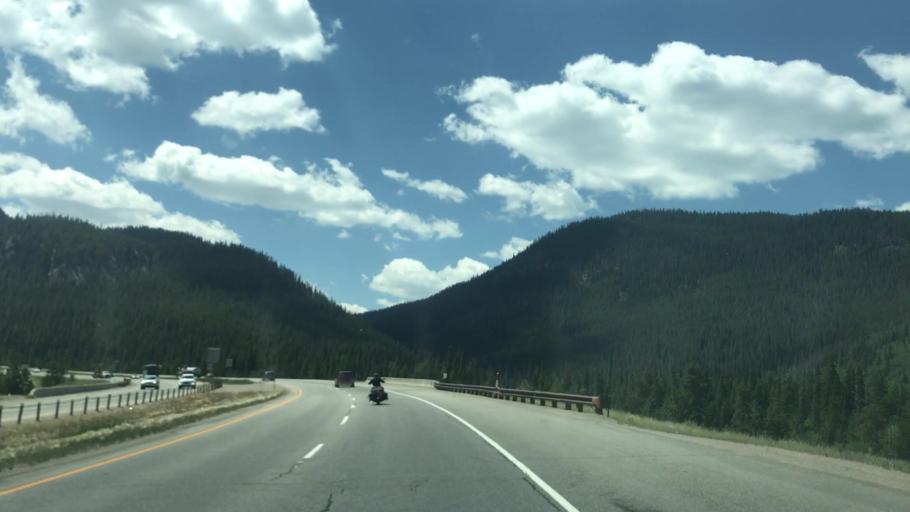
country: US
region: Colorado
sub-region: Summit County
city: Frisco
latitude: 39.5385
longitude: -106.1430
